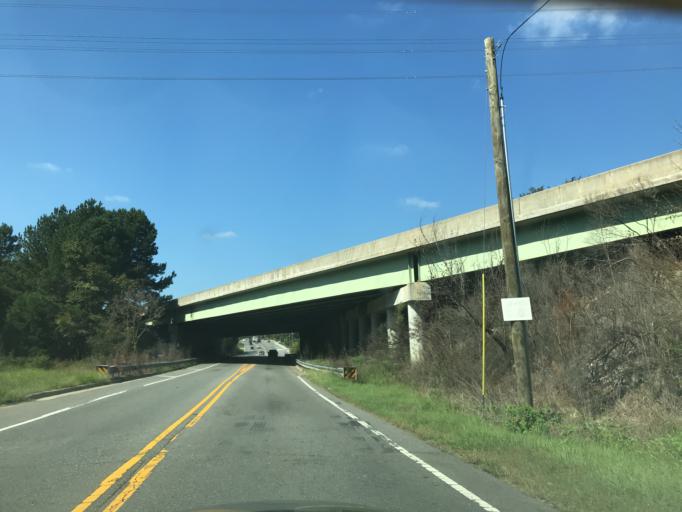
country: US
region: North Carolina
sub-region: Durham County
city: Durham
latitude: 35.9091
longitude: -78.9288
